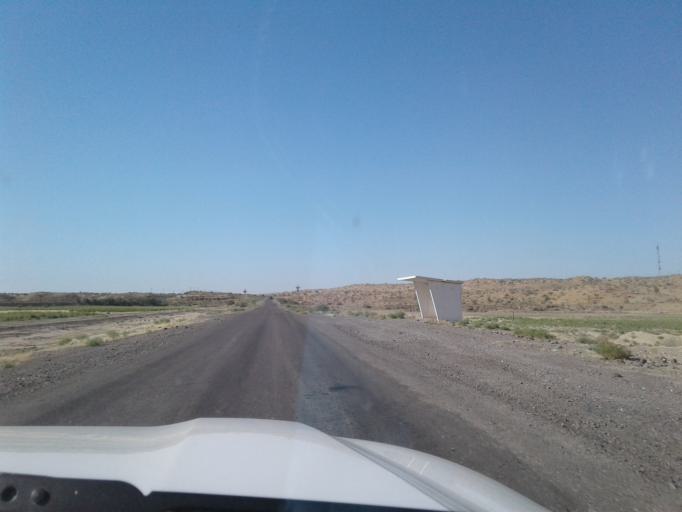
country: TM
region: Mary
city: Yoloeten
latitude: 36.6325
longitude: 62.4793
